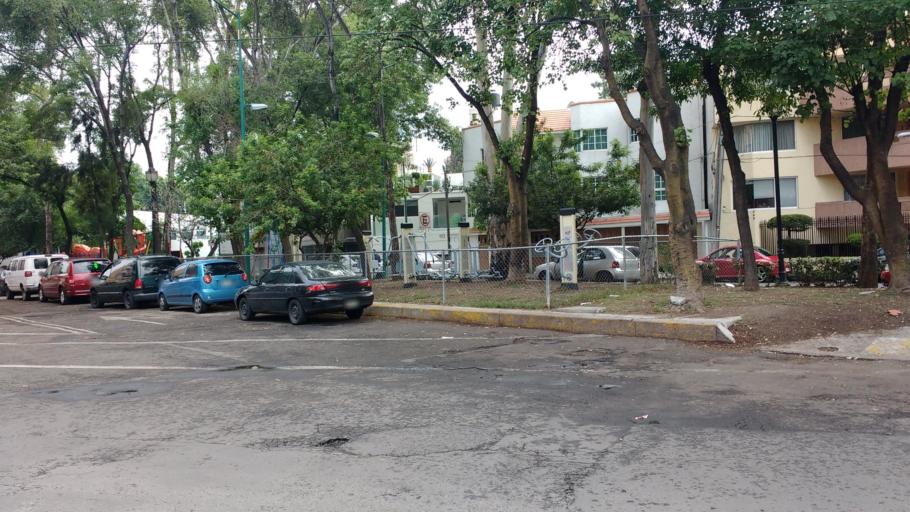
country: MX
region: Mexico City
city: Coyoacan
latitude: 19.3613
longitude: -99.1604
